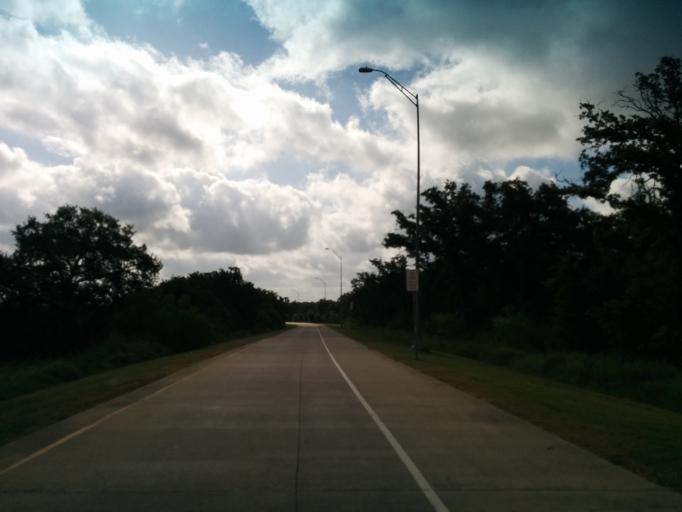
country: US
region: Texas
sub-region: Guadalupe County
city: Seguin
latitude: 29.6146
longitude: -97.8062
